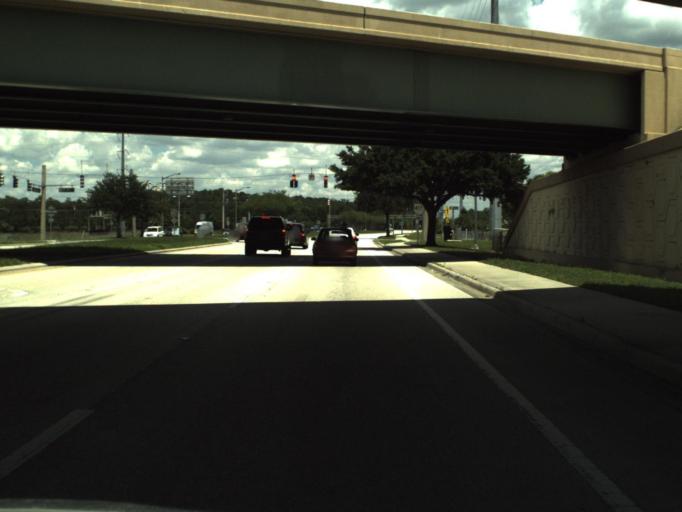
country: US
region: Florida
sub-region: Orange County
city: Meadow Woods
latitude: 28.4004
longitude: -81.2444
